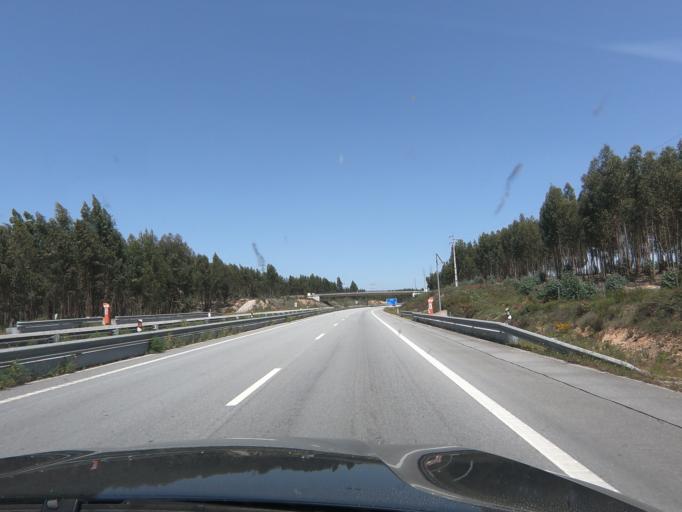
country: PT
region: Santarem
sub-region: Entroncamento
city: Entroncamento
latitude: 39.4980
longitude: -8.4392
